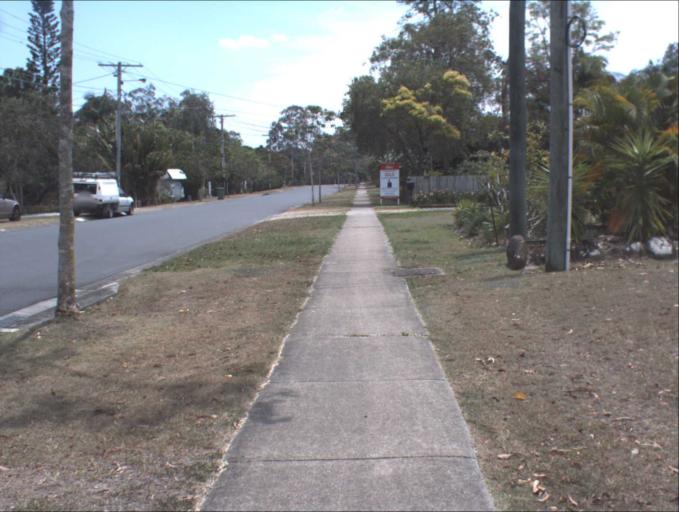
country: AU
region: Queensland
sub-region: Logan
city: Slacks Creek
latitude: -27.6703
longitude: 153.1834
